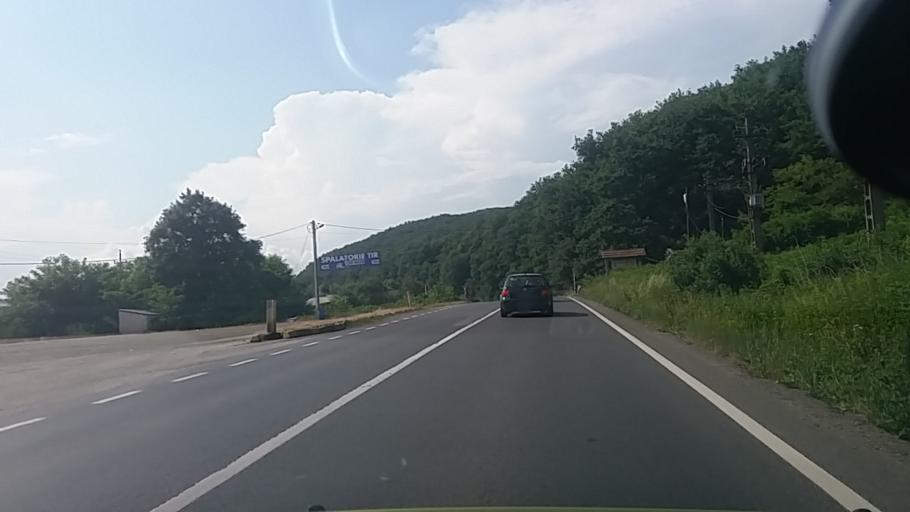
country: RO
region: Arad
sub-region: Comuna Bata
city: Bata
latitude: 46.0709
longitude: 22.0389
